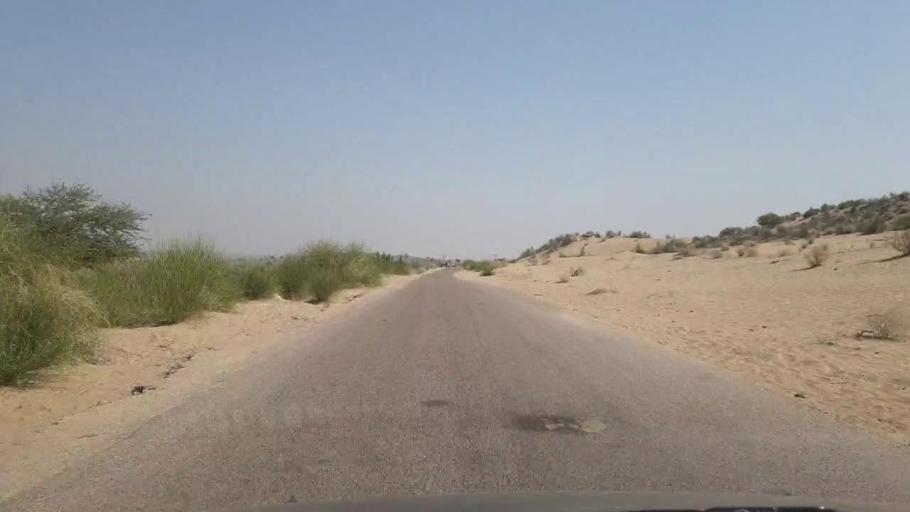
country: PK
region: Sindh
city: Chor
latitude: 25.6699
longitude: 70.1420
